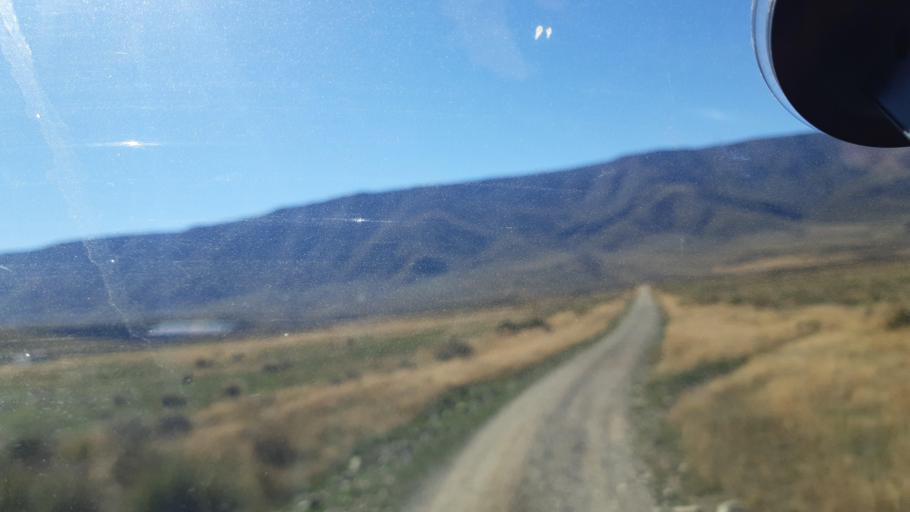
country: NZ
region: Otago
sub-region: Queenstown-Lakes District
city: Wanaka
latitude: -44.7779
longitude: 169.8892
